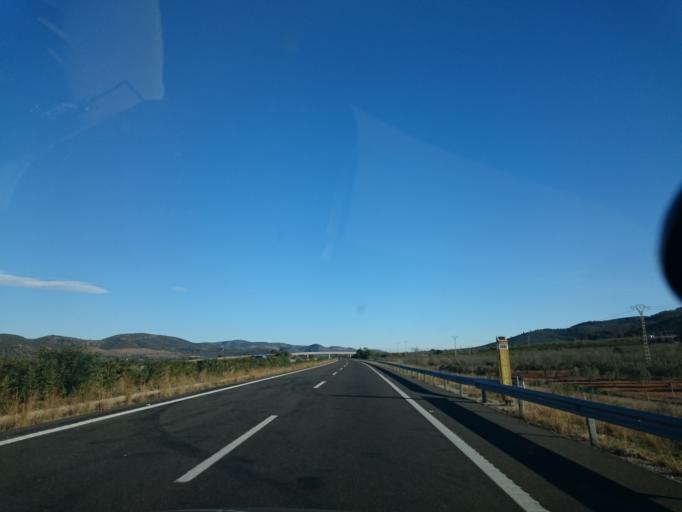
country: ES
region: Valencia
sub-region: Provincia de Castello
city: Alcala de Xivert
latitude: 40.3179
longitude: 0.2497
